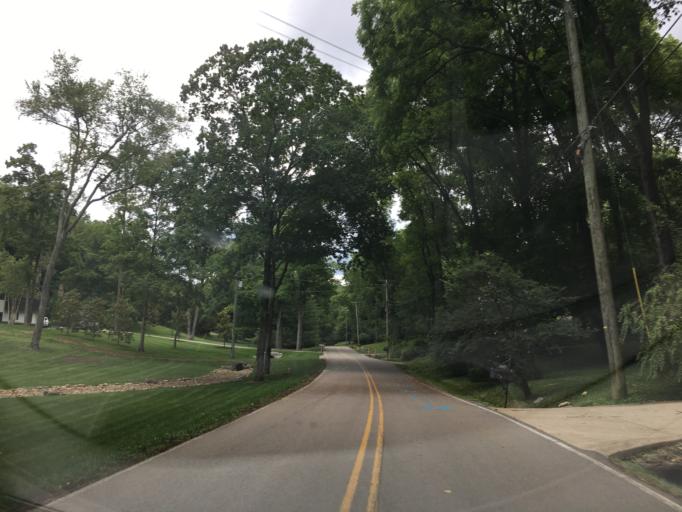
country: US
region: Tennessee
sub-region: Davidson County
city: Forest Hills
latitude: 36.0838
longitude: -86.8259
